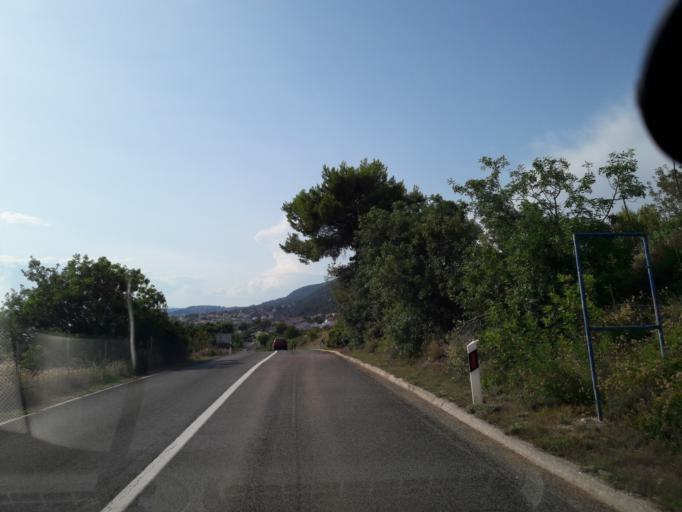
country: HR
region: Primorsko-Goranska
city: Banjol
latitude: 44.7229
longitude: 14.8210
